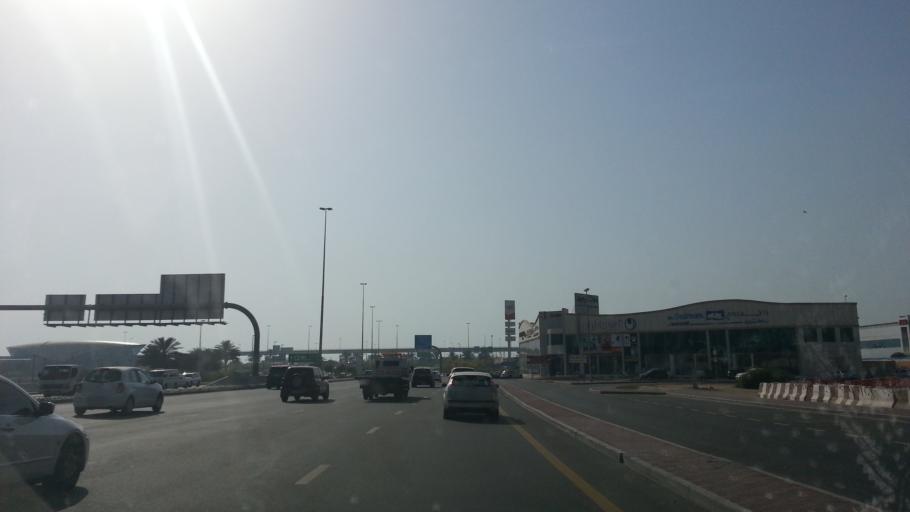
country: AE
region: Dubai
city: Dubai
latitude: 25.1200
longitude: 55.2068
